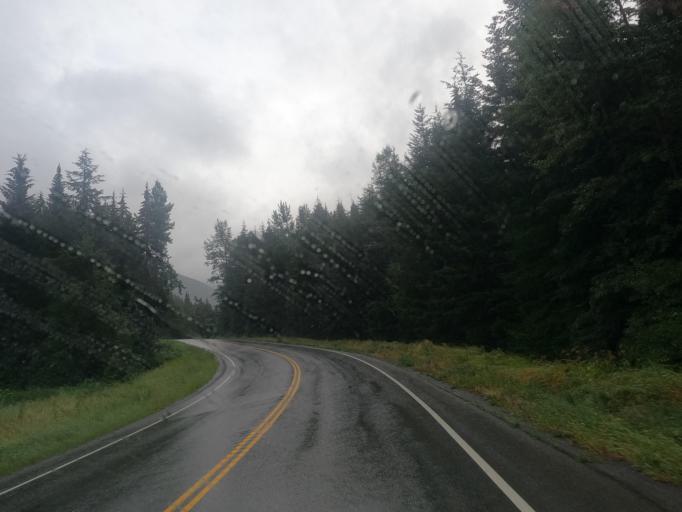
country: CA
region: British Columbia
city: Lillooet
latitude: 50.5315
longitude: -122.1556
